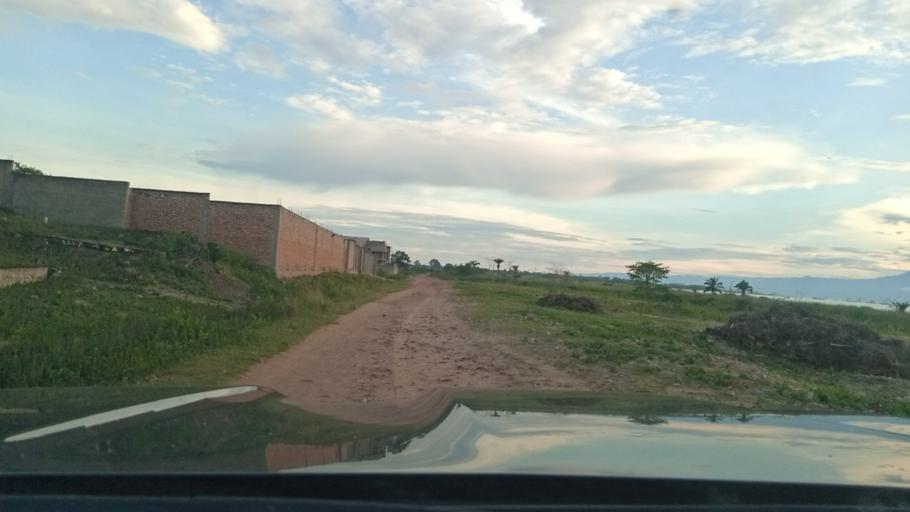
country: BI
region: Bujumbura Mairie
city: Bujumbura
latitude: -3.4598
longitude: 29.3438
